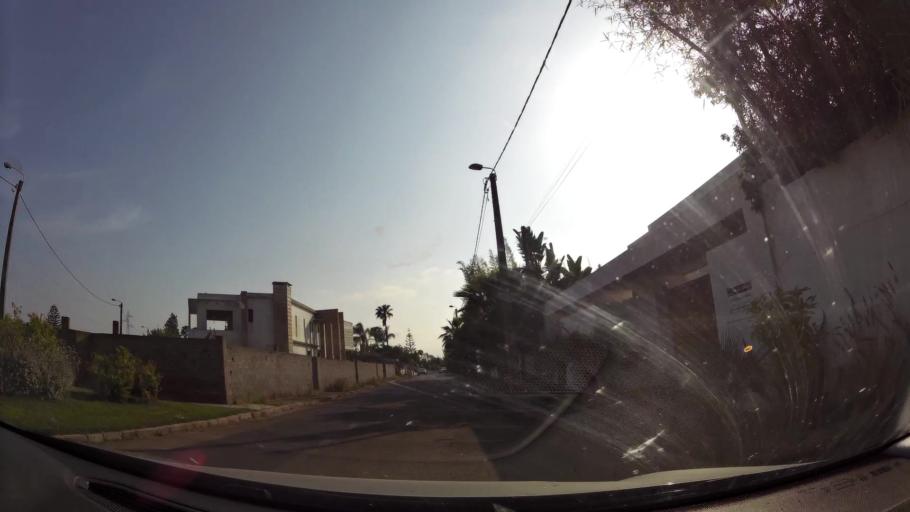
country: MA
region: Rabat-Sale-Zemmour-Zaer
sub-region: Rabat
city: Rabat
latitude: 33.9402
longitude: -6.8076
